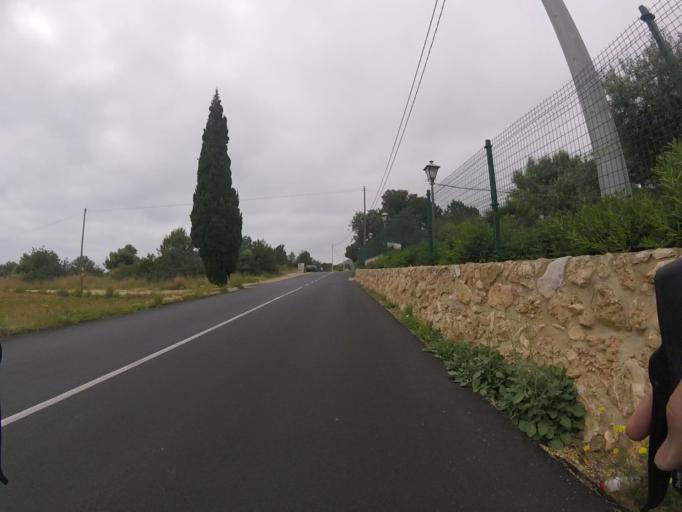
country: ES
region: Valencia
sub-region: Provincia de Castello
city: Peniscola
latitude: 40.3435
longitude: 0.3838
